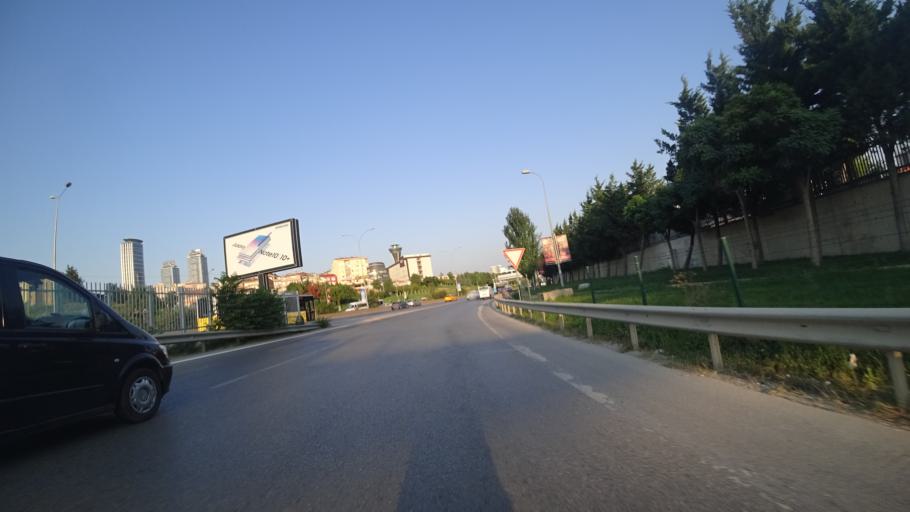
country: TR
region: Istanbul
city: UEskuedar
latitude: 40.9967
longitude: 29.0595
